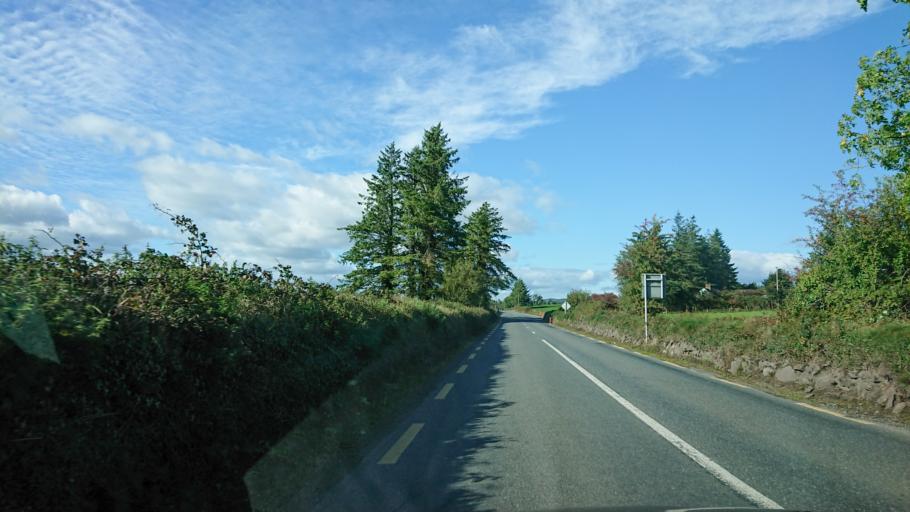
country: IE
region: Munster
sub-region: Waterford
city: Dungarvan
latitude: 52.1854
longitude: -7.6950
